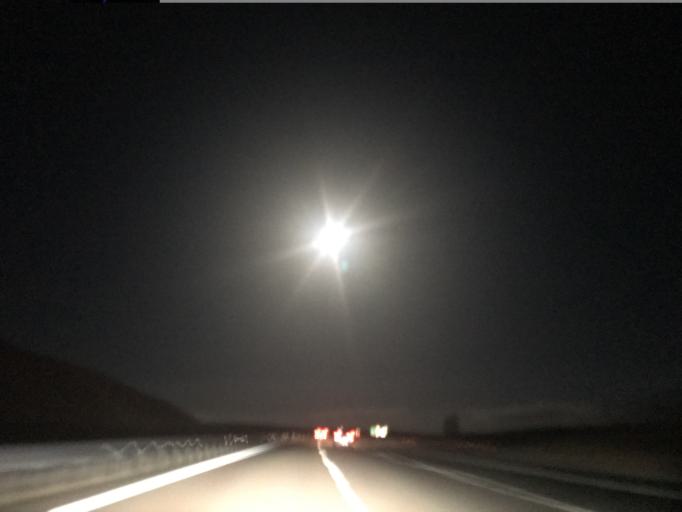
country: TR
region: Nigde
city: Ulukisla
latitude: 37.6362
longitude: 34.4958
